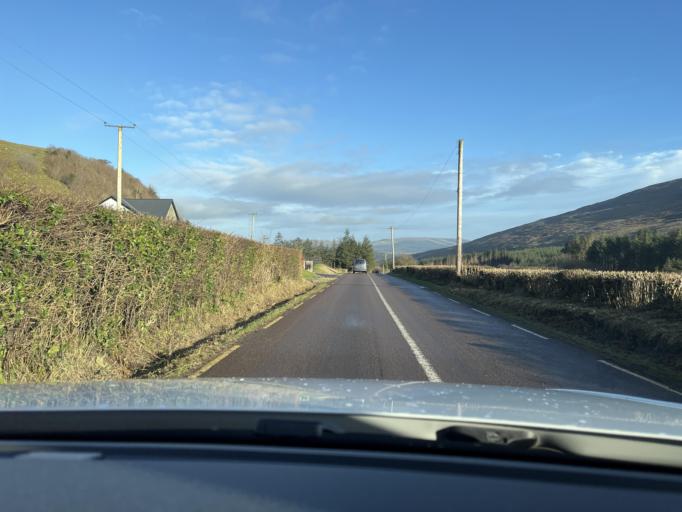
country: IE
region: Connaught
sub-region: County Leitrim
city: Manorhamilton
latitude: 54.2913
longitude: -8.2572
